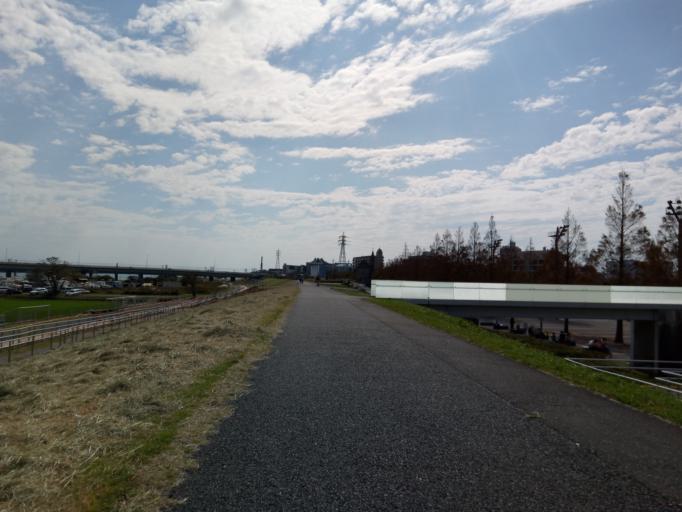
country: JP
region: Kanagawa
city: Hiratsuka
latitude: 35.3361
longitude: 139.3651
